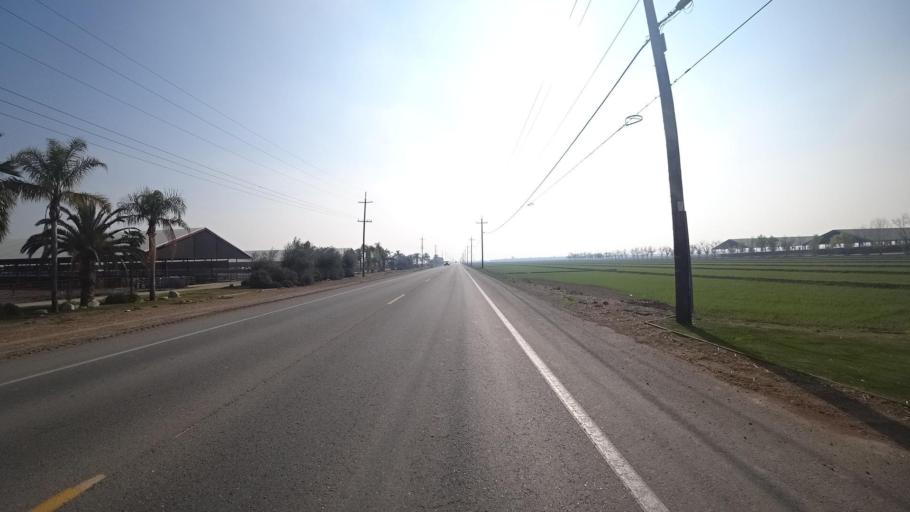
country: US
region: California
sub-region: Kern County
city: Greenfield
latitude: 35.1908
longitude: -119.1100
